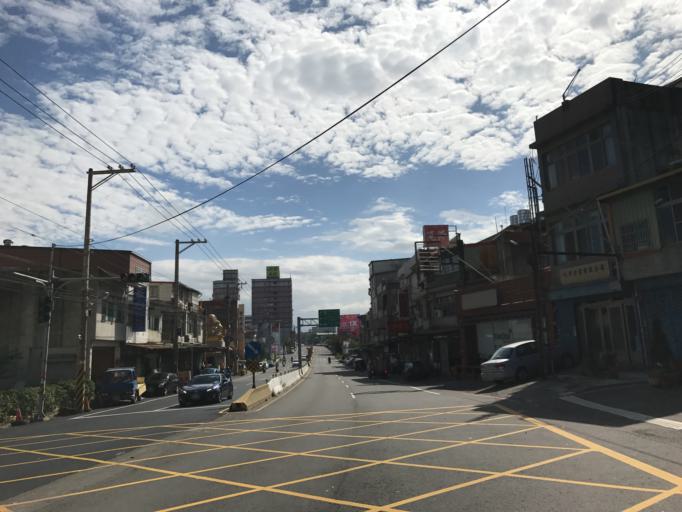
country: TW
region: Taiwan
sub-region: Hsinchu
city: Zhubei
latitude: 24.7726
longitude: 121.0494
